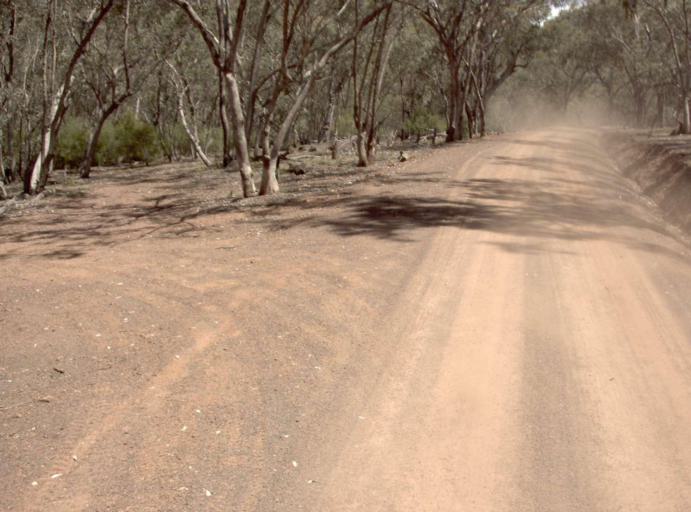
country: AU
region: New South Wales
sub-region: Snowy River
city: Jindabyne
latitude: -37.0893
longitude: 148.4126
